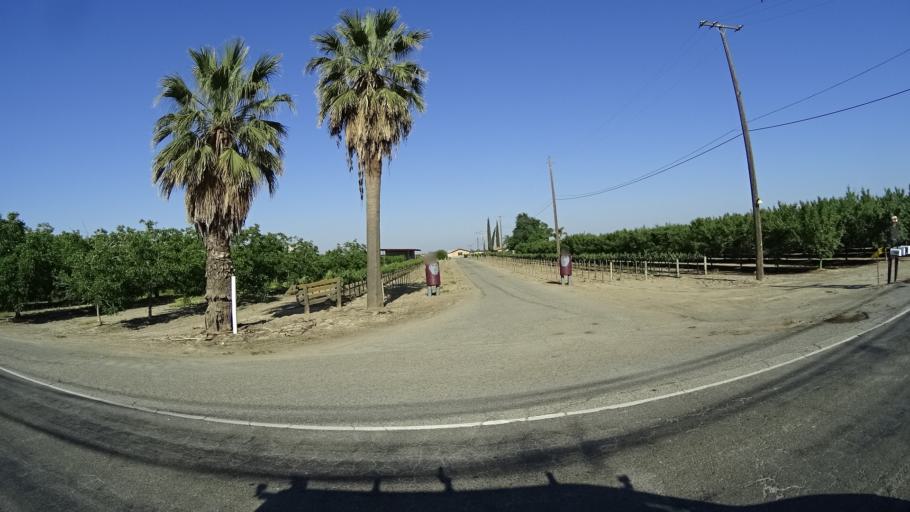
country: US
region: California
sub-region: Kings County
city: Armona
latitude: 36.3625
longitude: -119.7090
